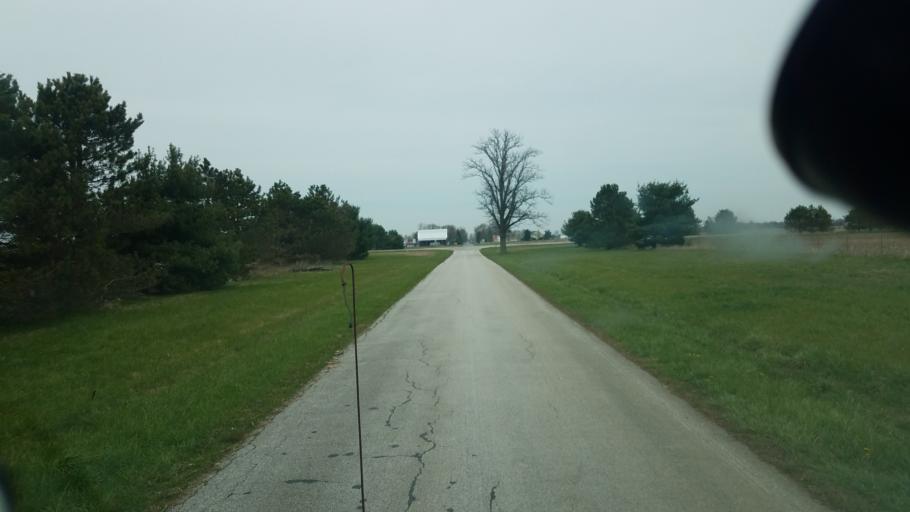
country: US
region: Ohio
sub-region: Wyandot County
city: Carey
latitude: 40.9636
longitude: -83.4768
